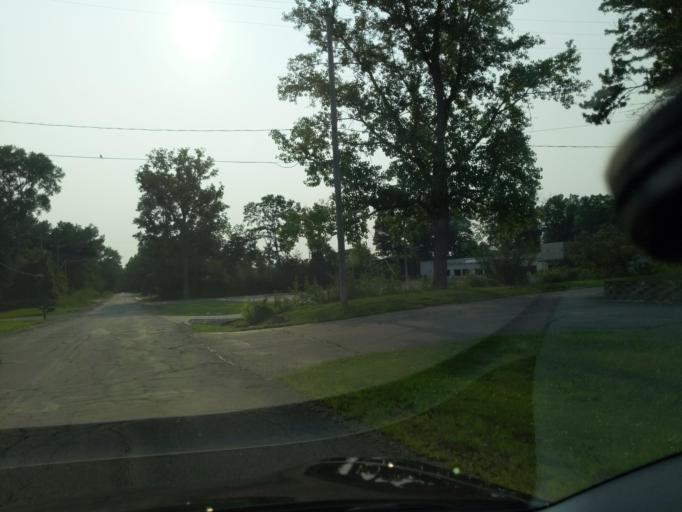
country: US
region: Michigan
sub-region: Jackson County
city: Jackson
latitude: 42.2710
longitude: -84.4574
